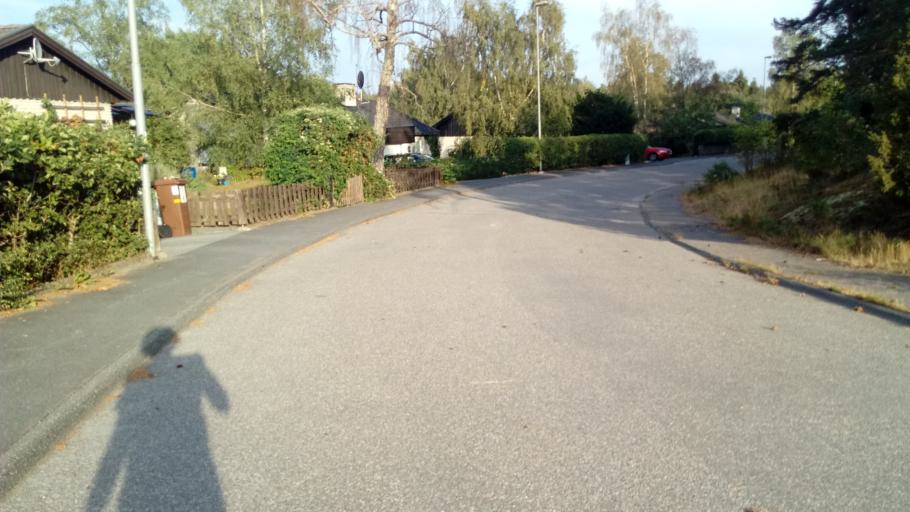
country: SE
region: Stockholm
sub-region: Tyreso Kommun
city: Bollmora
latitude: 59.2428
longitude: 18.2519
